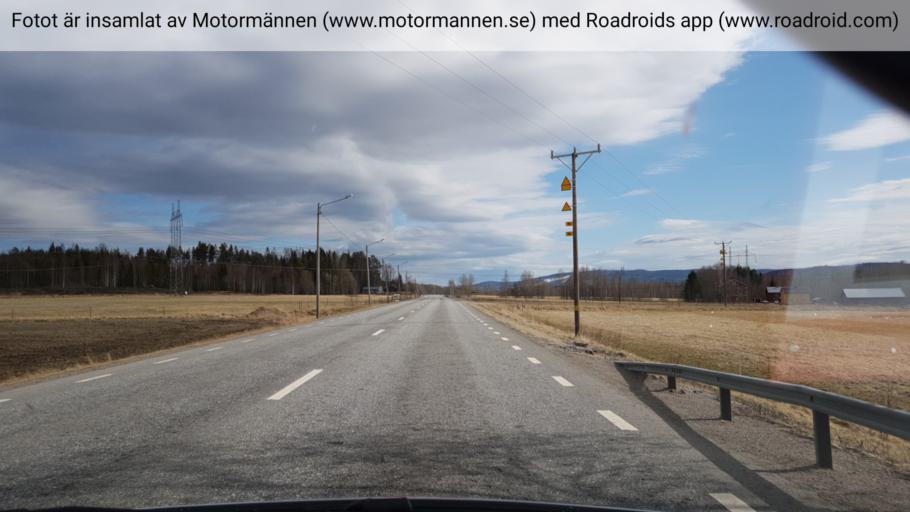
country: SE
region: Vaesternorrland
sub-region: Solleftea Kommun
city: Solleftea
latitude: 63.2365
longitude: 17.2106
